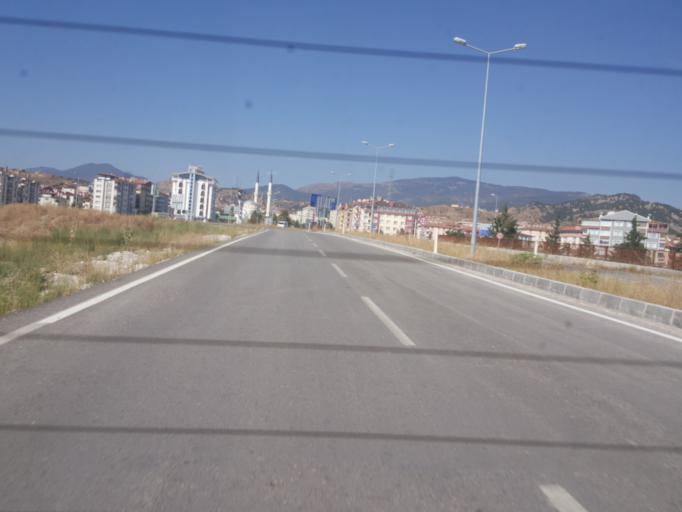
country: TR
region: Kastamonu
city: Tosya
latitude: 41.0072
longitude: 34.0602
